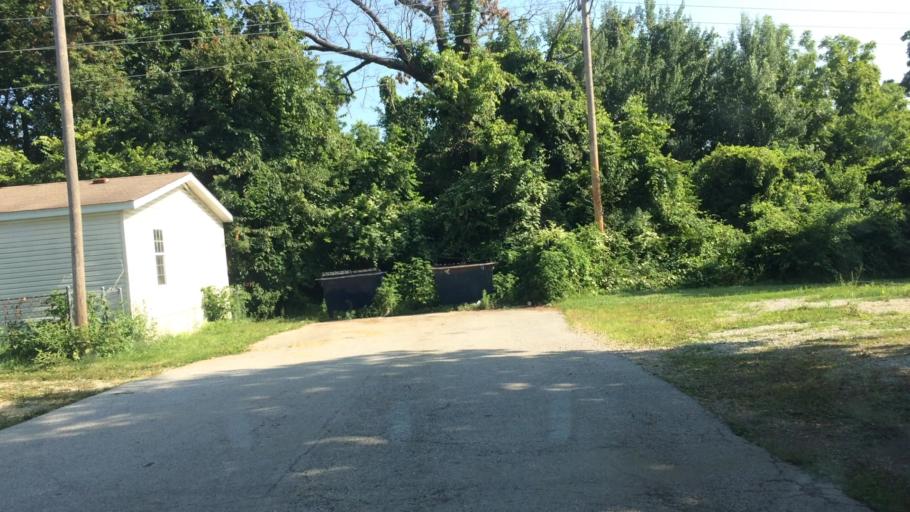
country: US
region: Missouri
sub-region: Greene County
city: Strafford
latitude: 37.2732
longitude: -93.0649
